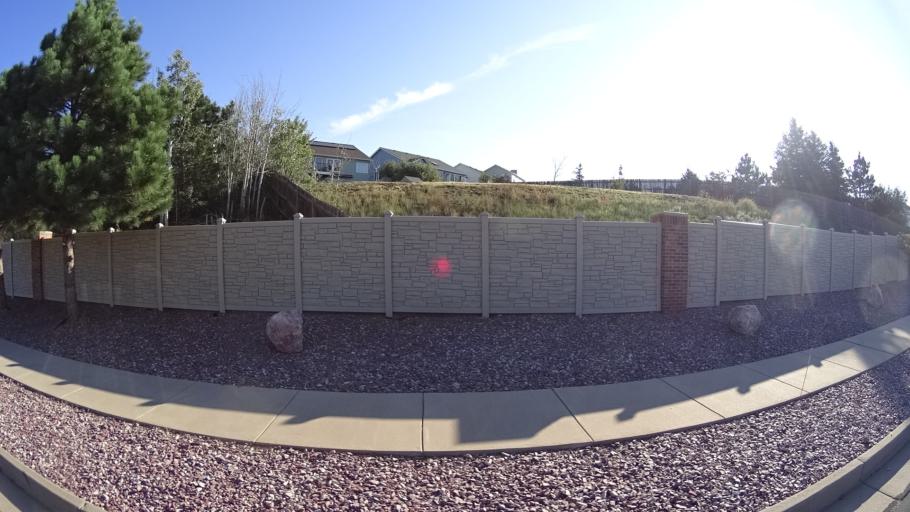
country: US
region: Colorado
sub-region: El Paso County
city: Cimarron Hills
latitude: 38.8896
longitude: -104.7014
